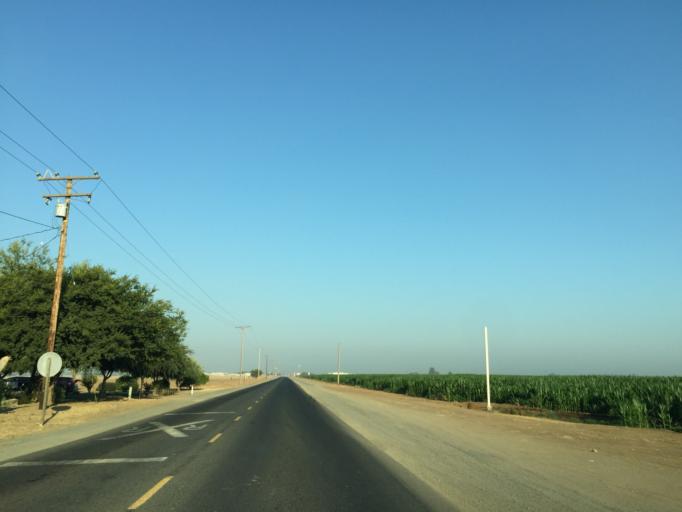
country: US
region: California
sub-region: Tulare County
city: Cutler
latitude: 36.4578
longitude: -119.3002
